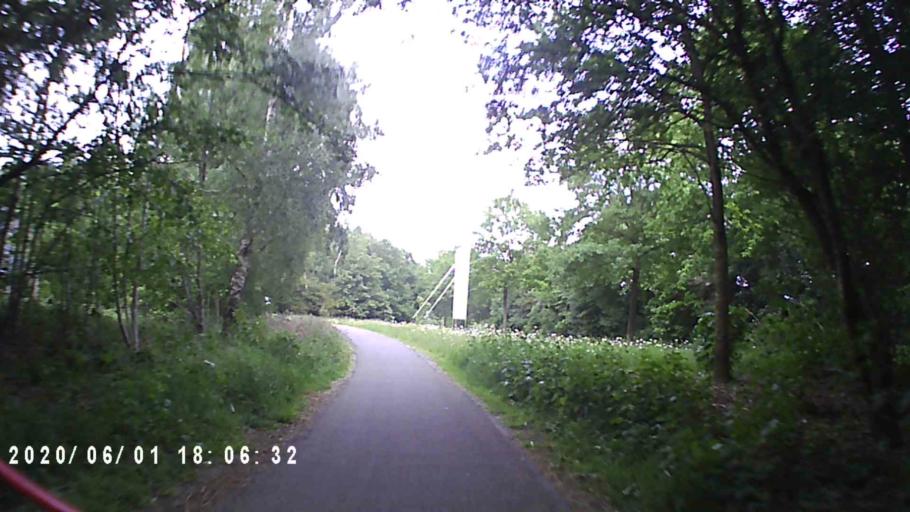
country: NL
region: Friesland
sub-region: Gemeente Tytsjerksteradiel
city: Sumar
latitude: 53.1798
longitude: 5.9958
